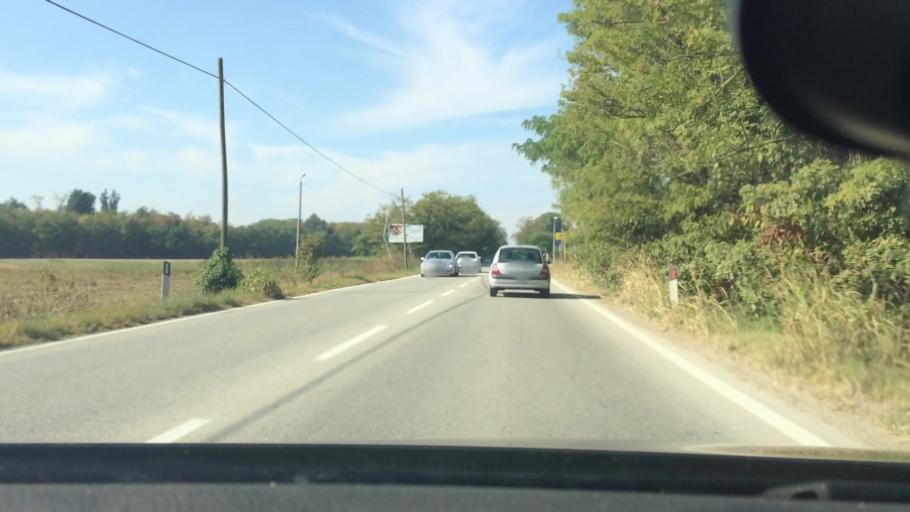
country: IT
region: Lombardy
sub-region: Provincia di Varese
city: Uboldo
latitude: 45.6131
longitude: 8.9818
